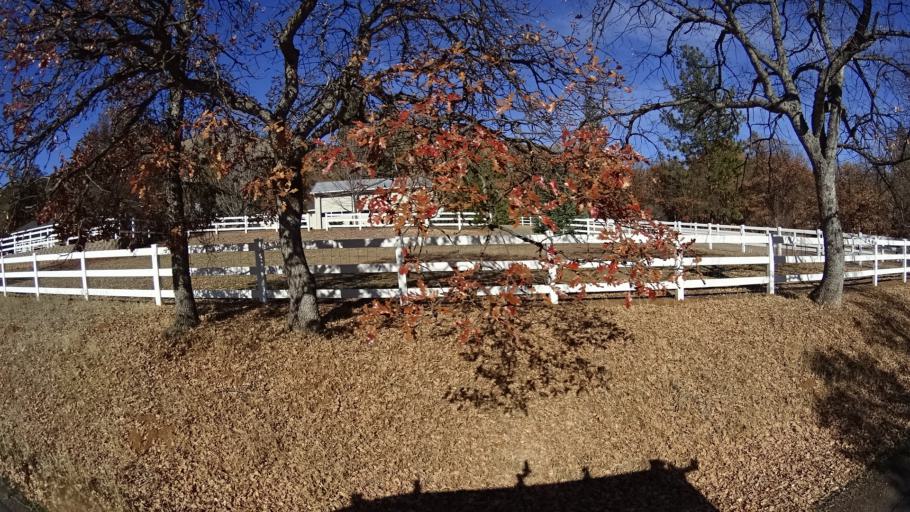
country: US
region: California
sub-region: Siskiyou County
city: Yreka
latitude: 41.7170
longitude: -122.6659
